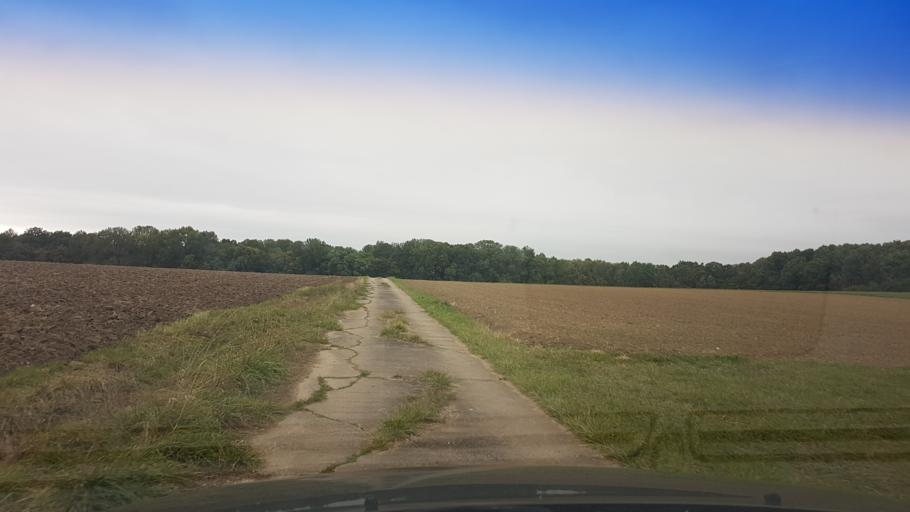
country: DE
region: Bavaria
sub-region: Upper Franconia
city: Memmelsdorf
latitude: 49.9338
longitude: 10.9768
